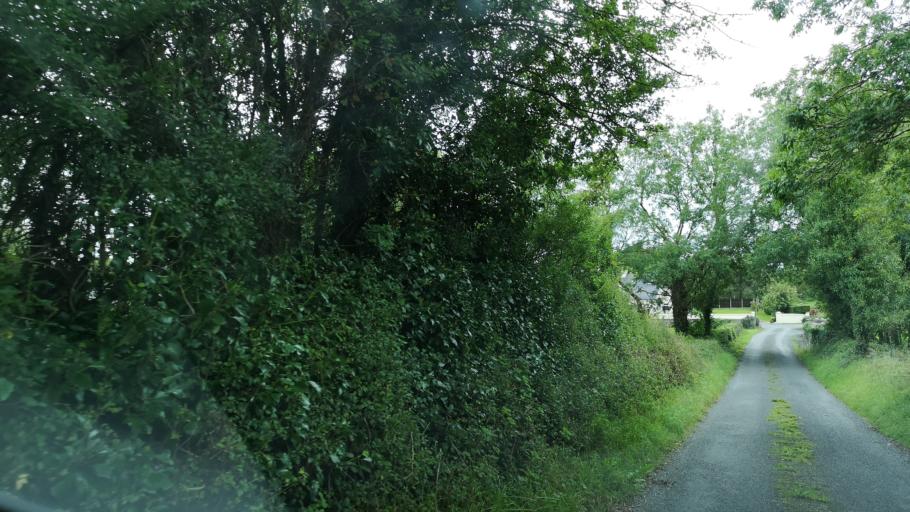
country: IE
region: Connaught
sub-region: County Galway
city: Loughrea
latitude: 53.1605
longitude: -8.4700
